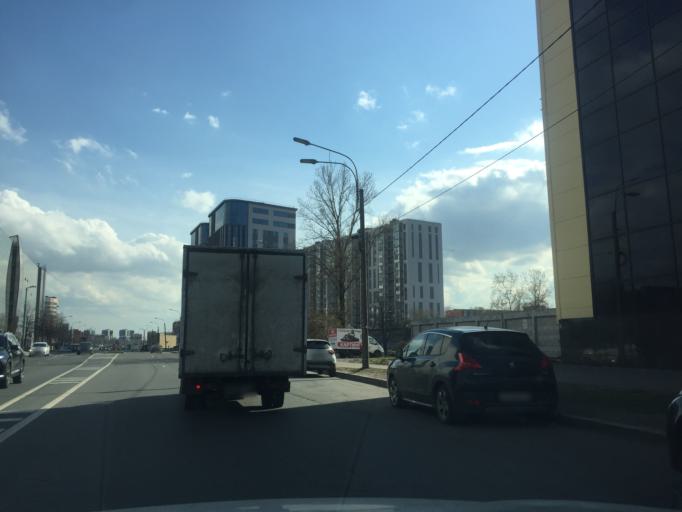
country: RU
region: St.-Petersburg
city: Krasnogvargeisky
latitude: 59.9374
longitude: 30.4352
